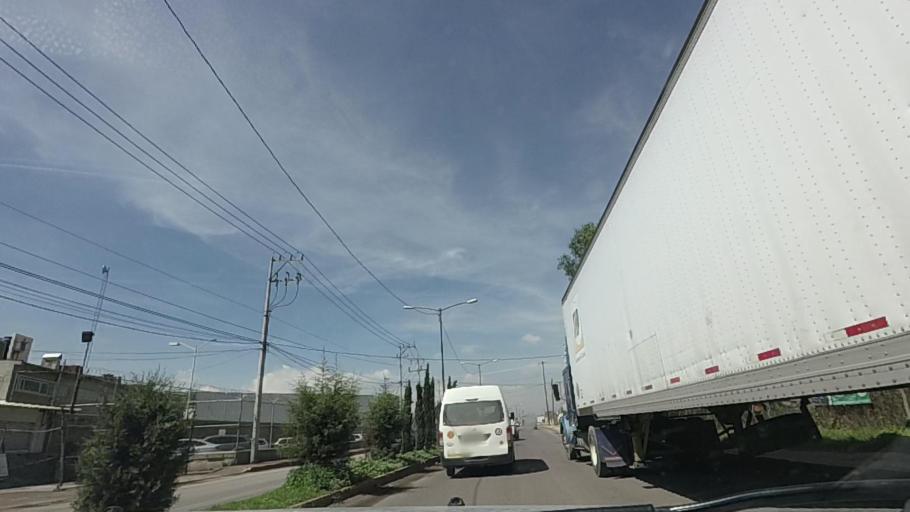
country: MX
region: Mexico
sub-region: Cuautitlan
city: San Jose del Puente
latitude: 19.7226
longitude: -99.1904
